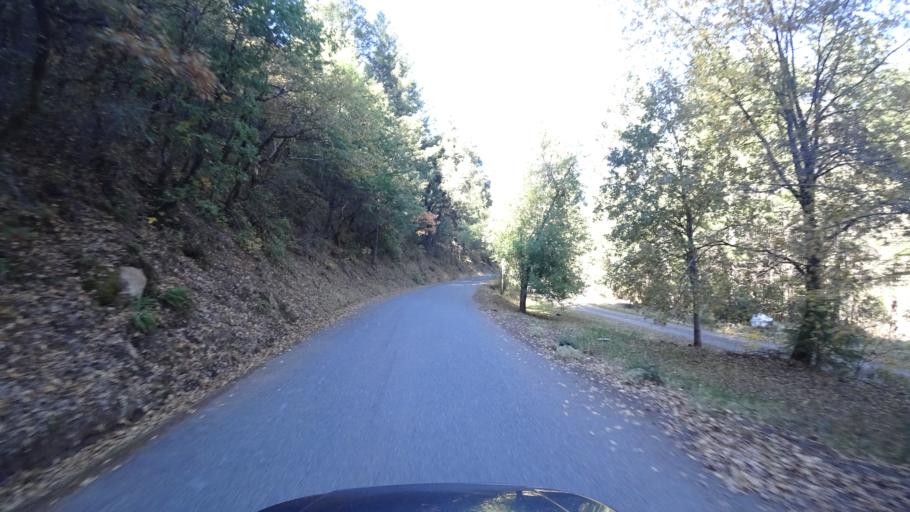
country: US
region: California
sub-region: Humboldt County
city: Willow Creek
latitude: 41.2486
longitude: -123.3031
